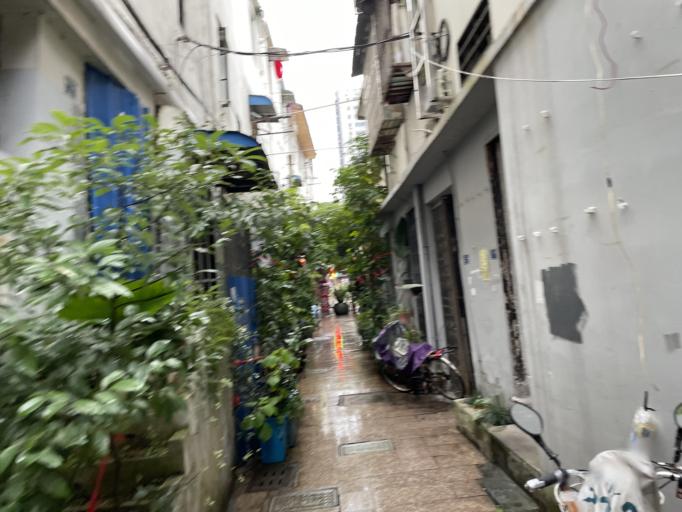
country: CN
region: Zhejiang Sheng
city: Wuma
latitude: 28.0157
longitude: 120.6576
